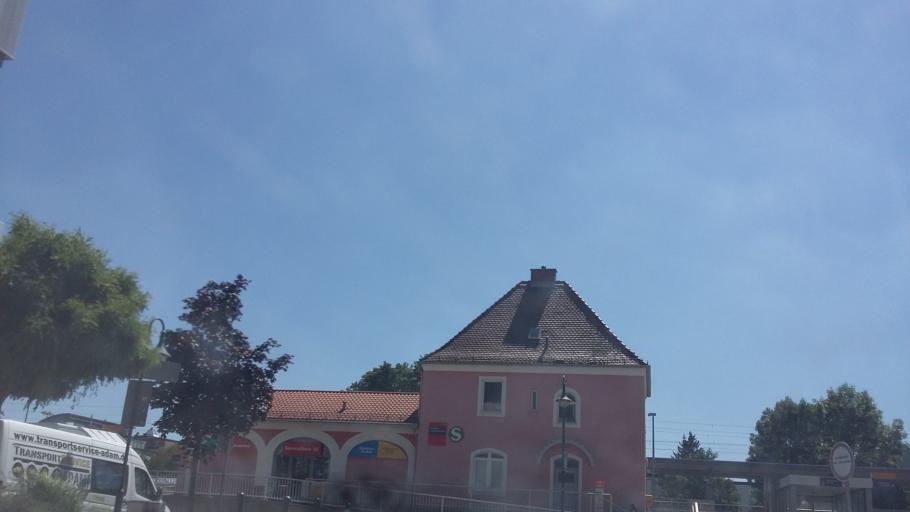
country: DE
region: Bavaria
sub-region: Upper Bavaria
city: Germering
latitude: 48.1294
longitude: 11.3637
